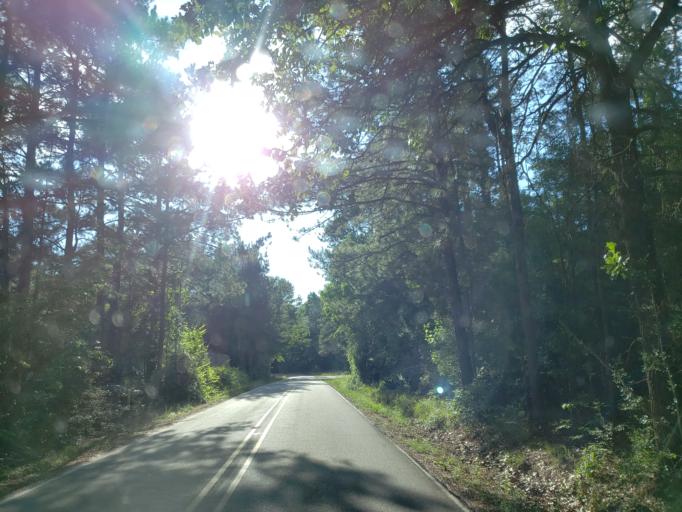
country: US
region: Mississippi
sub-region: Forrest County
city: Petal
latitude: 31.3268
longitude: -89.2124
